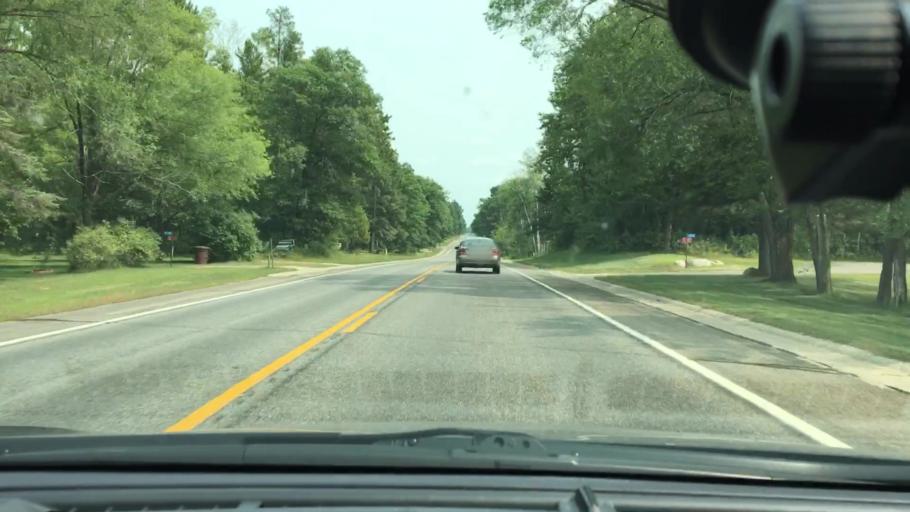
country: US
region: Minnesota
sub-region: Cass County
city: East Gull Lake
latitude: 46.4128
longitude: -94.3127
